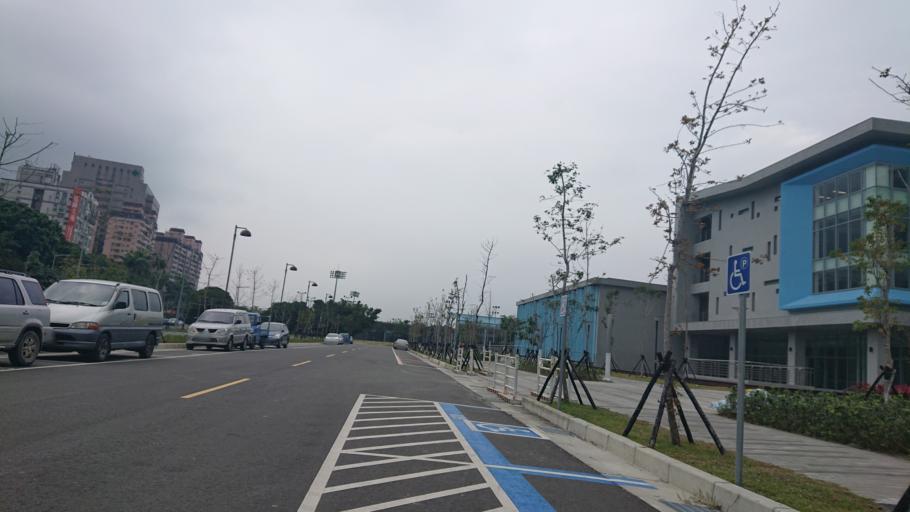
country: TW
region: Taiwan
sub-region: Taoyuan
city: Taoyuan
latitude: 24.9396
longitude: 121.3666
